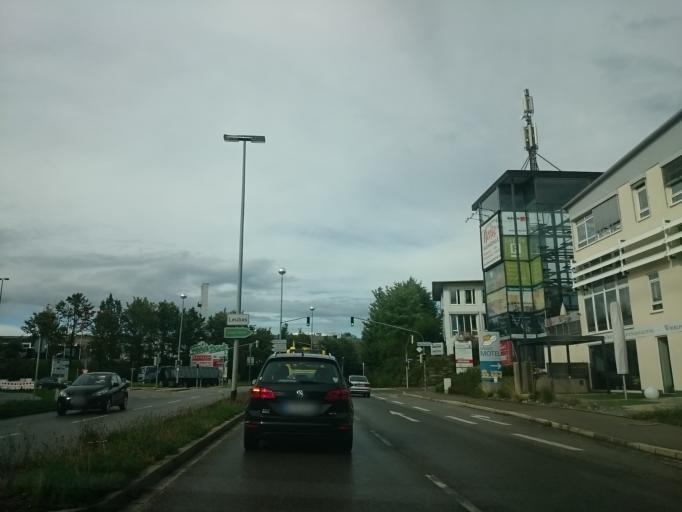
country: DE
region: Bavaria
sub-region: Swabia
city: Kempten (Allgaeu)
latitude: 47.7462
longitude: 10.3234
